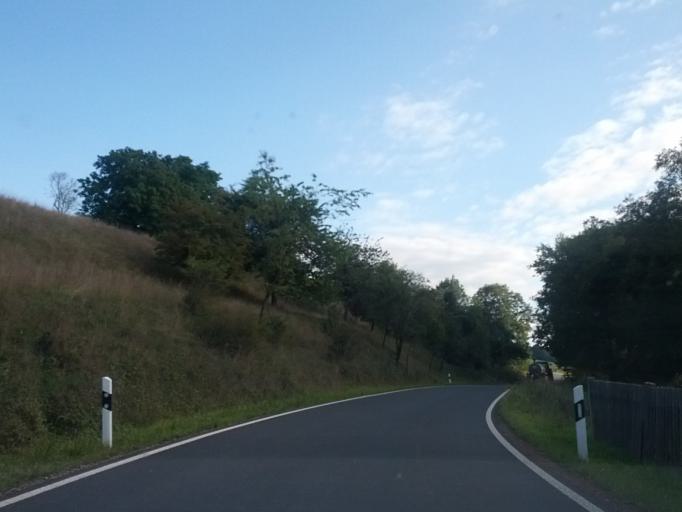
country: DE
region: Thuringia
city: Lauchroden
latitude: 50.9861
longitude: 10.1591
